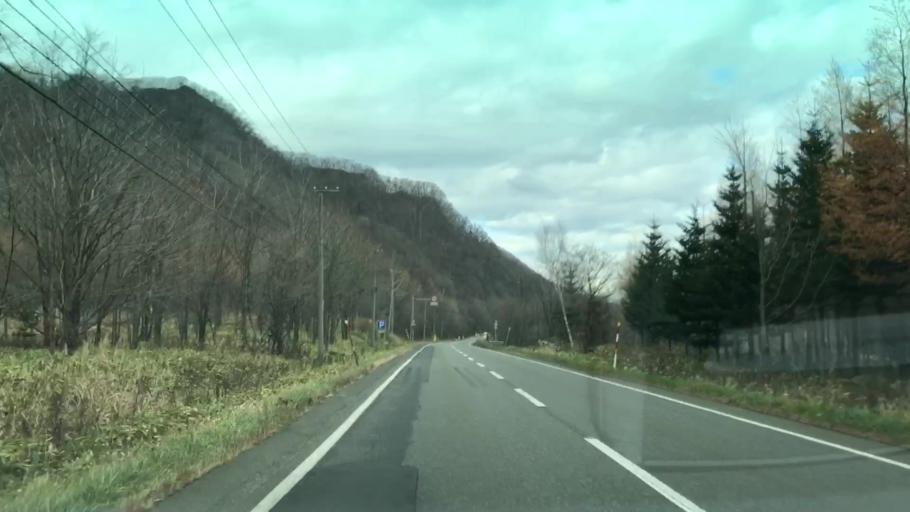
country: JP
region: Hokkaido
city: Shizunai-furukawacho
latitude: 42.8343
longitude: 142.4157
